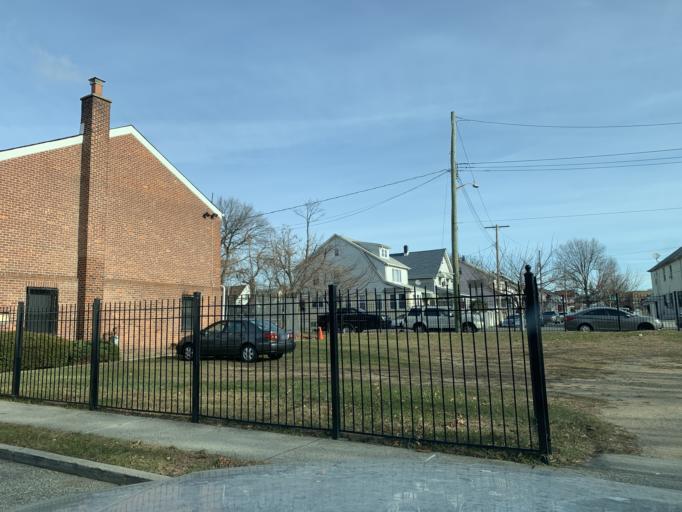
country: US
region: New York
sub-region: Queens County
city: Jamaica
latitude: 40.6941
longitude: -73.7856
